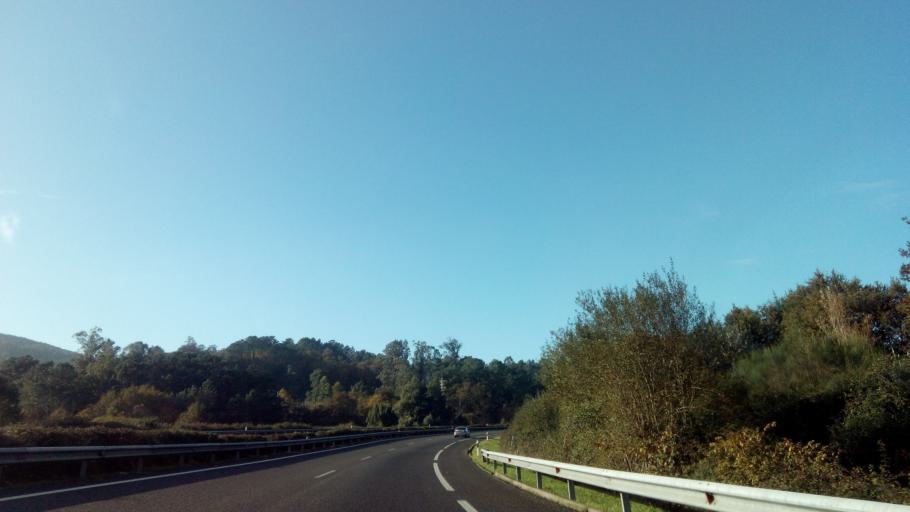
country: ES
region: Galicia
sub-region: Provincia de Pontevedra
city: Ponteareas
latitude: 42.1619
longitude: -8.5301
